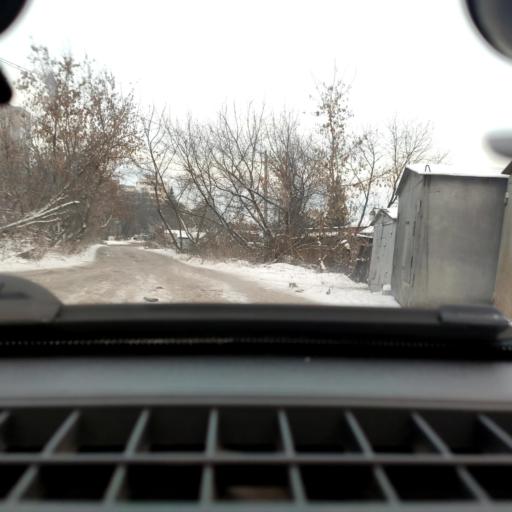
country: RU
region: Bashkortostan
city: Ufa
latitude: 54.8085
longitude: 56.1388
